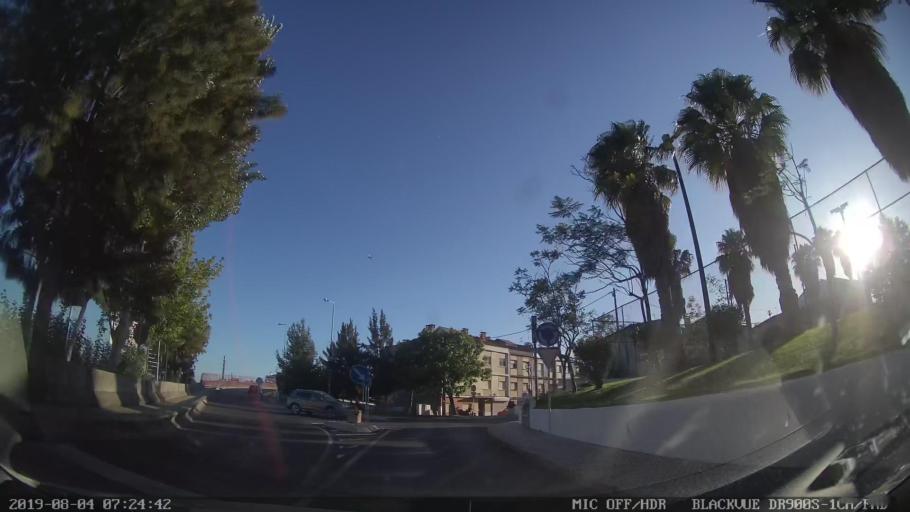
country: PT
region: Lisbon
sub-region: Loures
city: Santa Iria da Azoia
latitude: 38.8487
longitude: -9.0823
